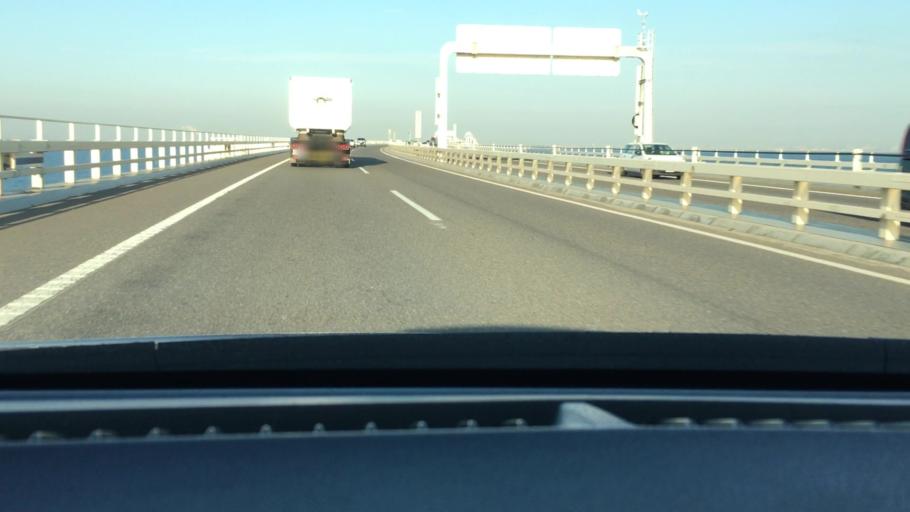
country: JP
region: Chiba
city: Kisarazu
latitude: 35.4378
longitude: 139.9136
